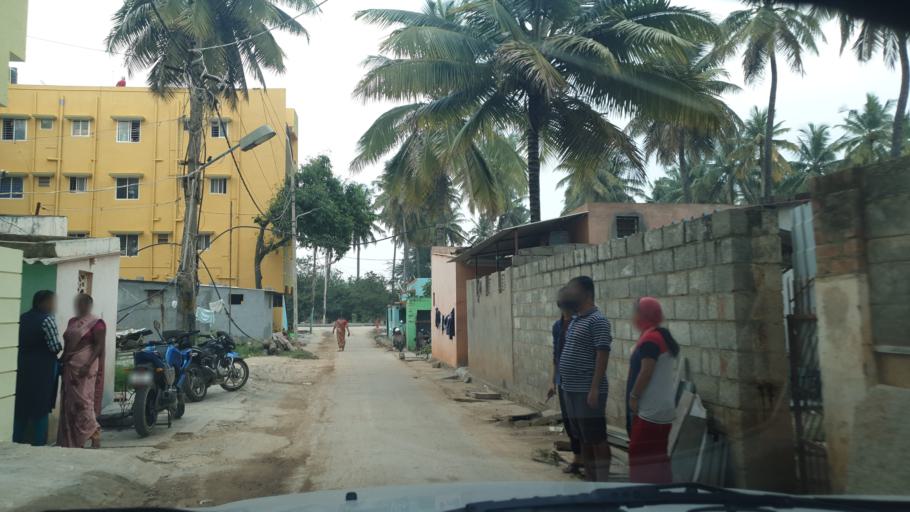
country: IN
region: Karnataka
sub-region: Bangalore Urban
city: Bangalore
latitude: 12.9398
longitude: 77.7053
